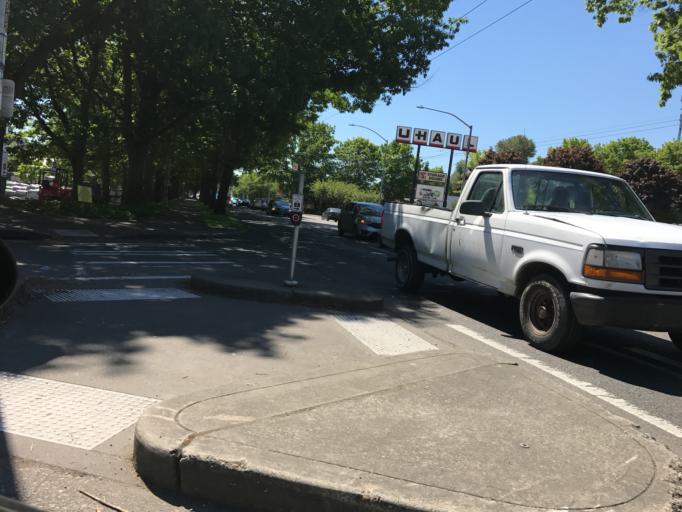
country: US
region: Washington
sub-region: King County
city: Seattle
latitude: 47.5810
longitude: -122.3001
